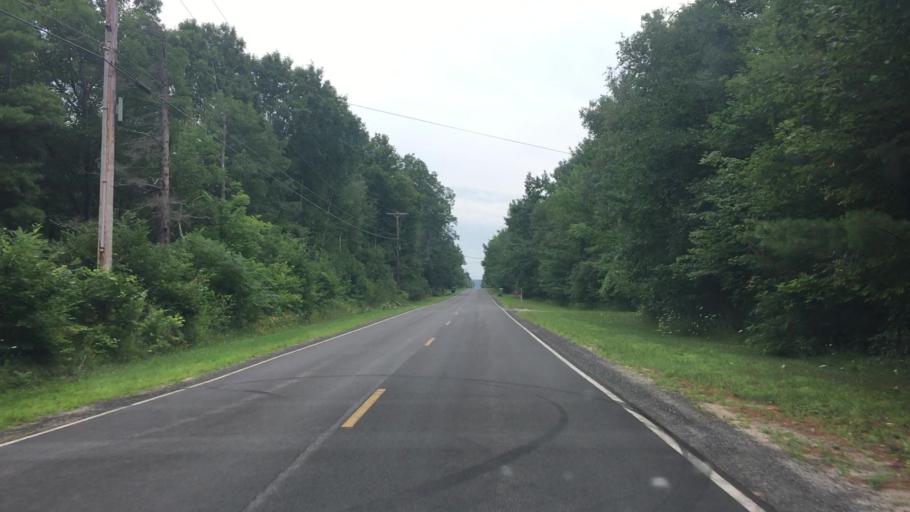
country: US
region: New York
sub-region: Clinton County
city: Peru
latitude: 44.5935
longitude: -73.6268
